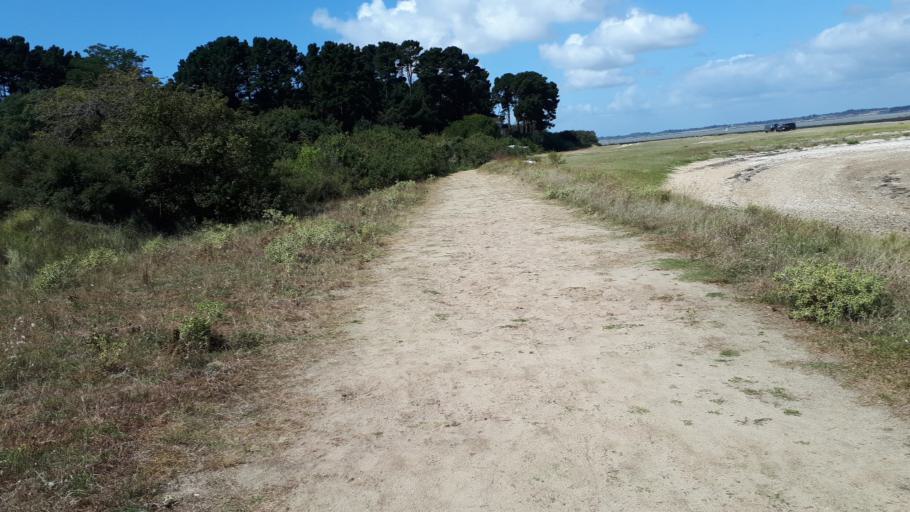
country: FR
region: Brittany
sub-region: Departement du Morbihan
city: Penestin
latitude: 47.4949
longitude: -2.4880
